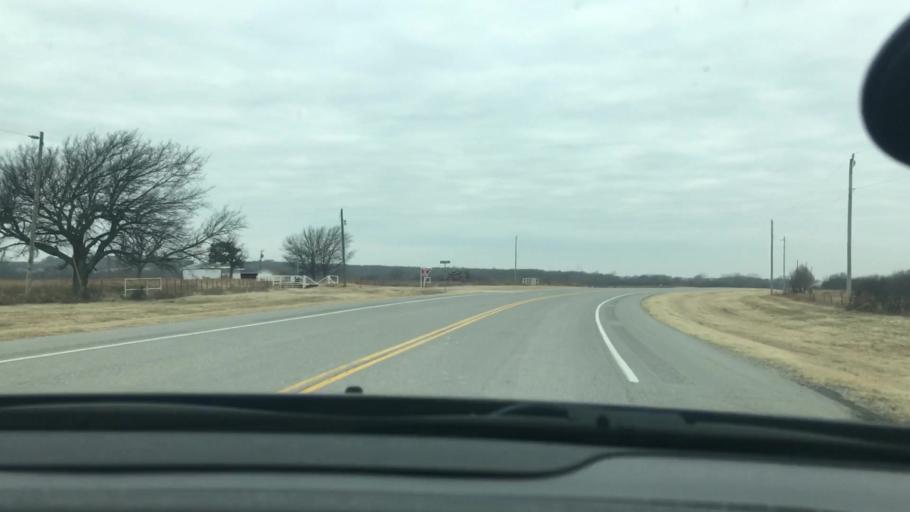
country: US
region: Oklahoma
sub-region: Murray County
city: Davis
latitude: 34.4930
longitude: -97.3702
